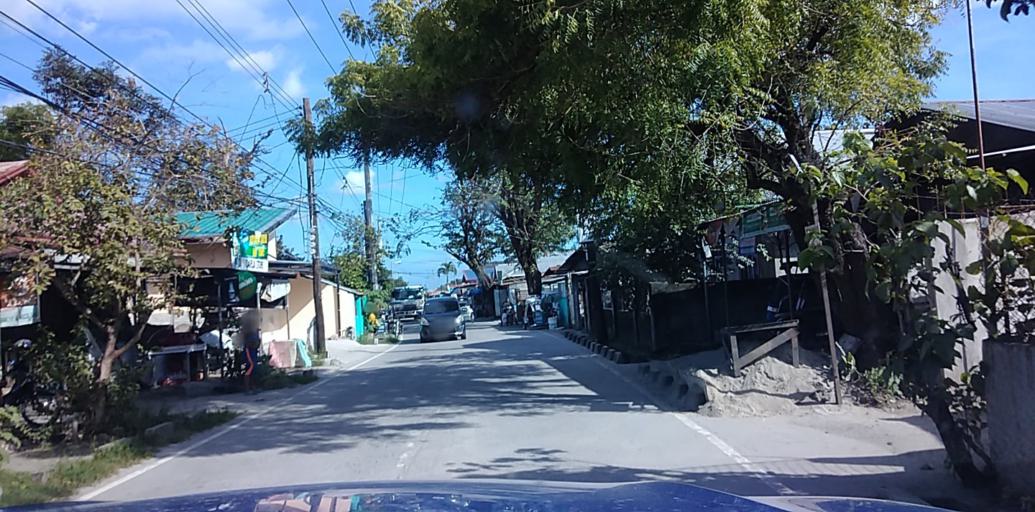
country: PH
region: Central Luzon
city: Santol
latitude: 15.1460
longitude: 120.5499
